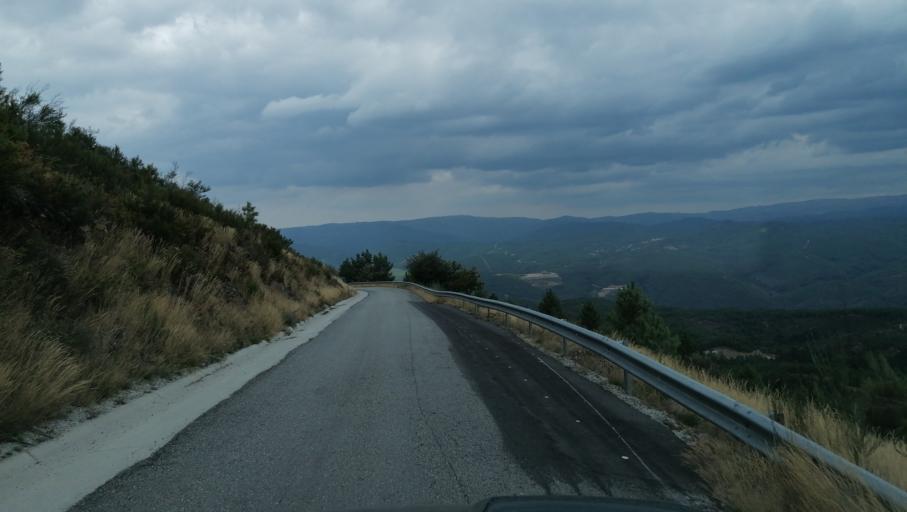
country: PT
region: Vila Real
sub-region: Vila Pouca de Aguiar
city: Vila Pouca de Aguiar
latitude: 41.5595
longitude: -7.6964
